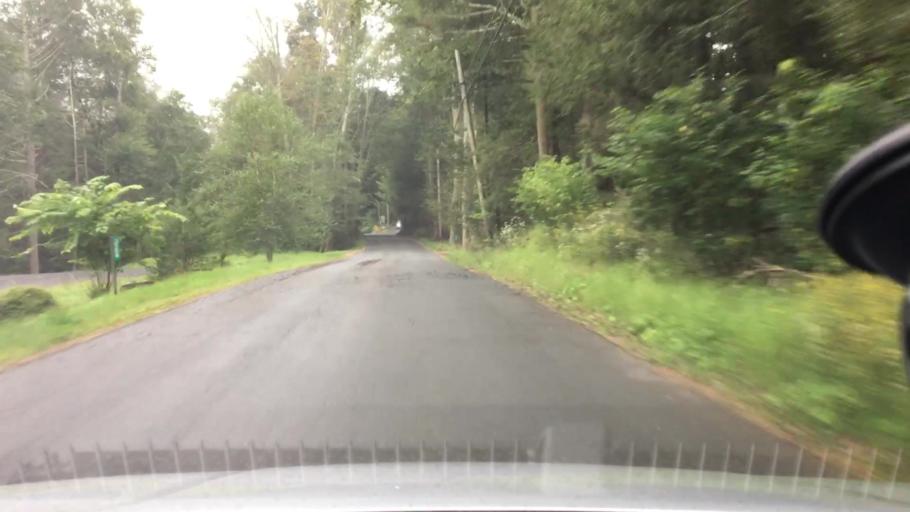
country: US
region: Pennsylvania
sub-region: Monroe County
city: Mountainhome
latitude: 41.1650
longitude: -75.2689
